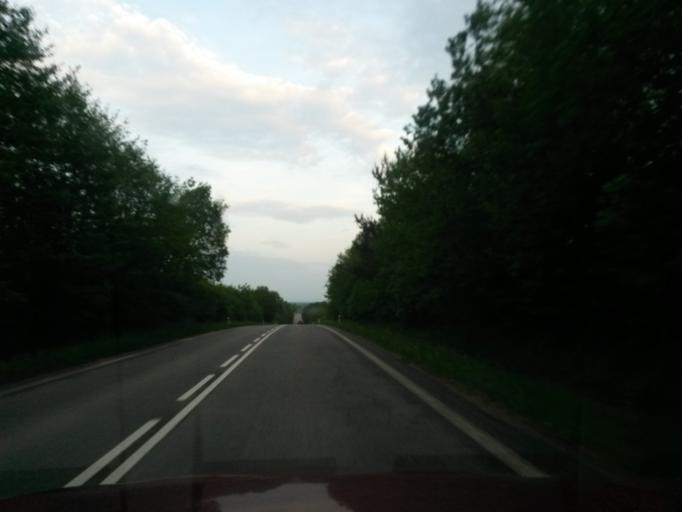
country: SK
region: Kosicky
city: Moldava nad Bodvou
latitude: 48.6891
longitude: 21.0585
